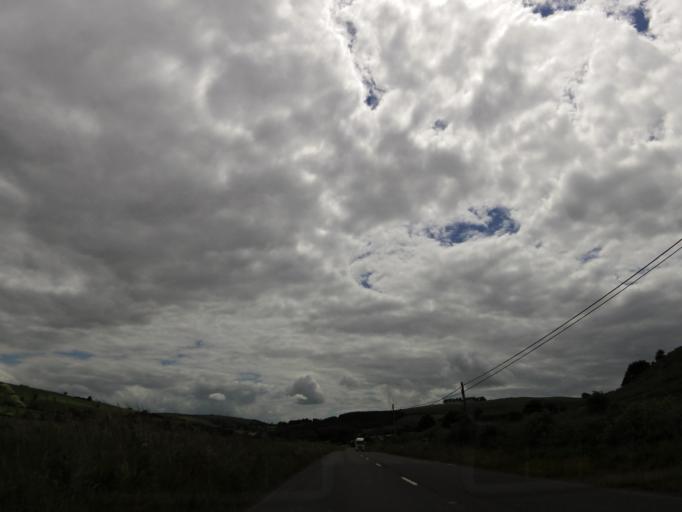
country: IE
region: Munster
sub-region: North Tipperary
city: Templemore
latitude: 52.7611
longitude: -8.0146
